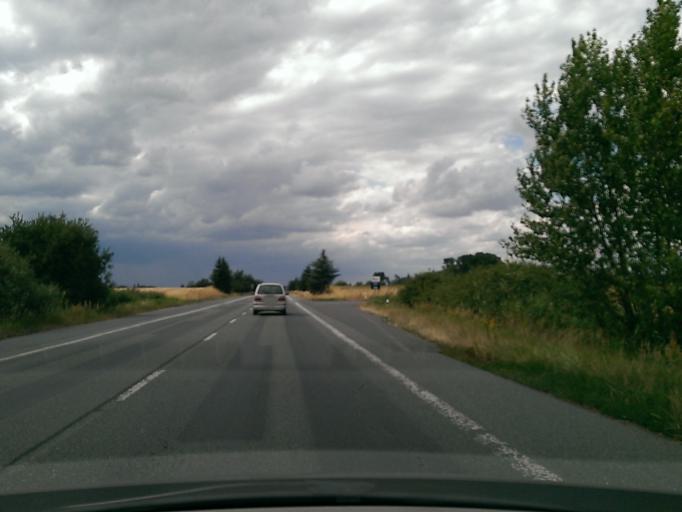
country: CZ
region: Central Bohemia
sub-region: Okres Nymburk
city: Podebrady
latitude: 50.1237
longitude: 15.1137
